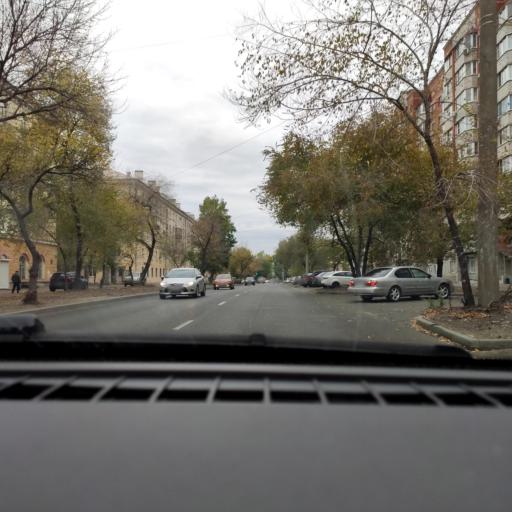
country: RU
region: Voronezj
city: Voronezh
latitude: 51.6369
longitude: 39.2382
